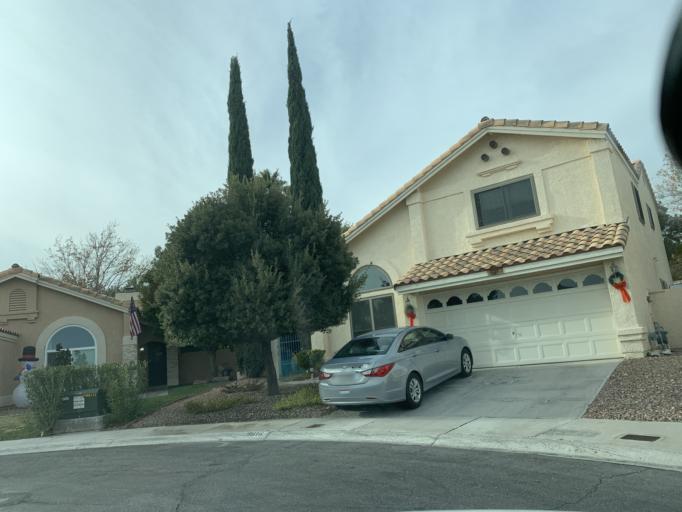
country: US
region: Nevada
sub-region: Clark County
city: Summerlin South
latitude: 36.1419
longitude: -115.3054
